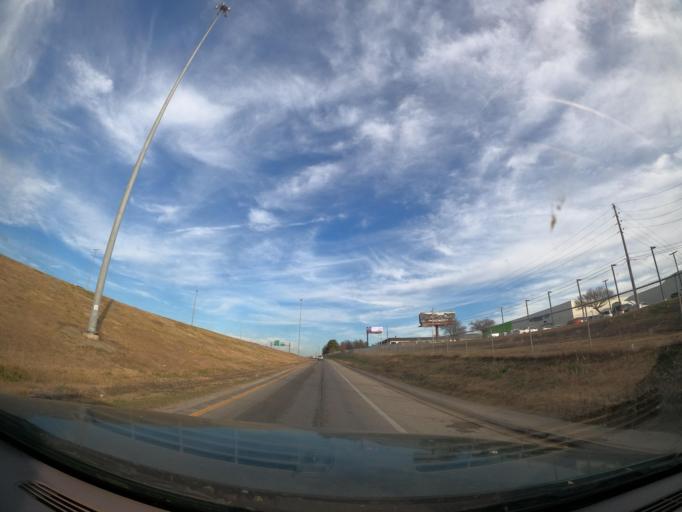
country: US
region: Oklahoma
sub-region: Tulsa County
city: Jenks
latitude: 36.0250
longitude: -95.8857
